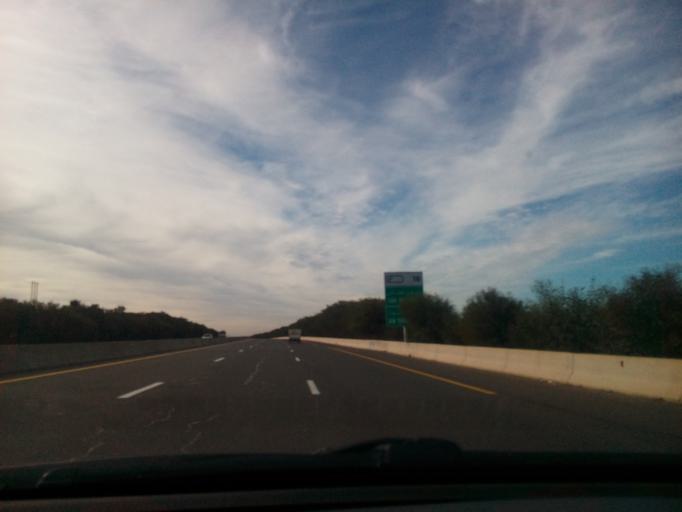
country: DZ
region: Sidi Bel Abbes
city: Sidi Bel Abbes
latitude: 35.2139
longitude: -0.6823
